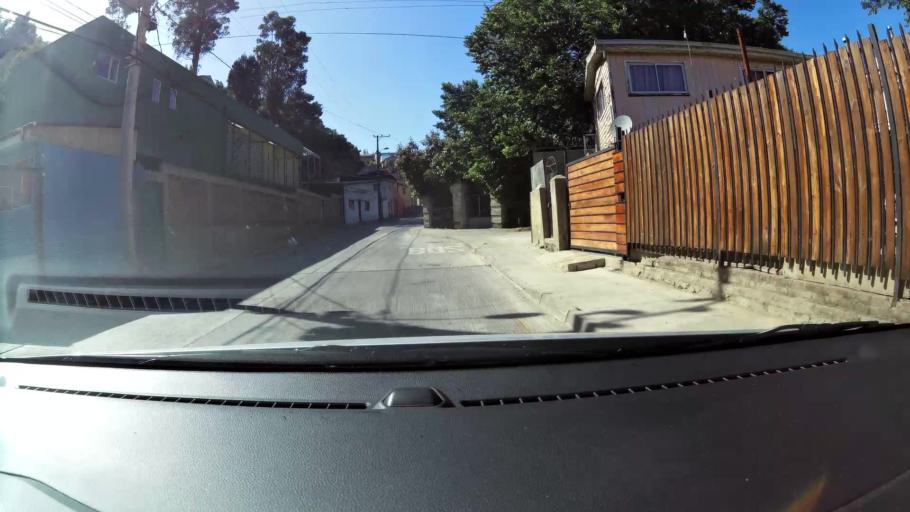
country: CL
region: Valparaiso
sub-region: Provincia de Valparaiso
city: Valparaiso
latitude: -33.0614
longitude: -71.5909
